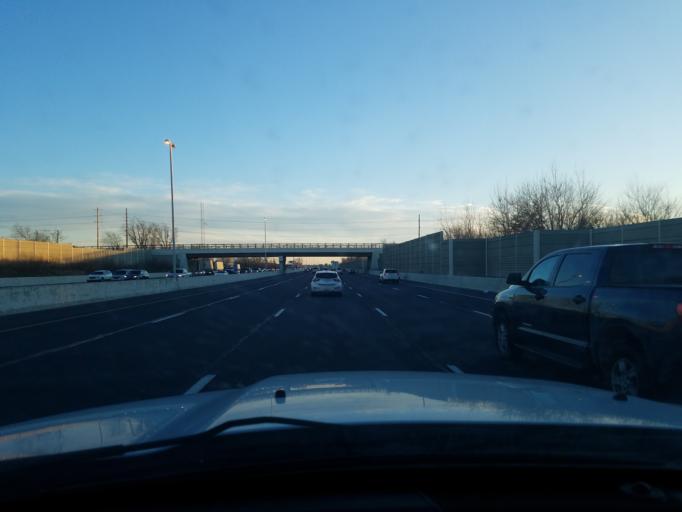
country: US
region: Indiana
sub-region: Marion County
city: Speedway
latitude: 39.8396
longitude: -86.2762
